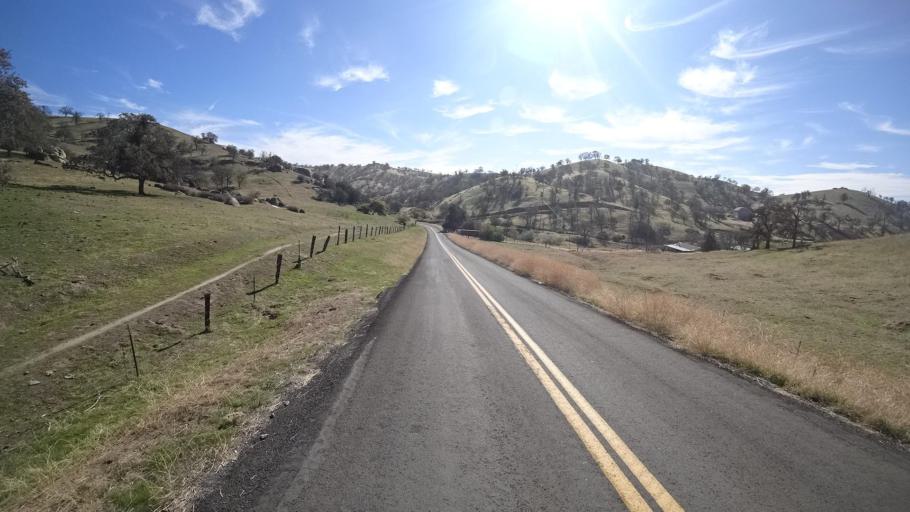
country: US
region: California
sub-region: Kern County
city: Oildale
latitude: 35.6573
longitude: -118.8423
